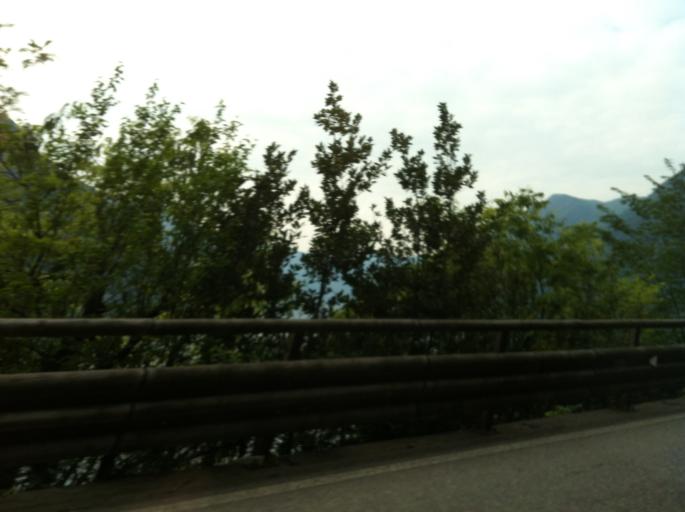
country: IT
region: Lombardy
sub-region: Provincia di Como
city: Colonno
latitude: 45.9512
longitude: 9.1398
